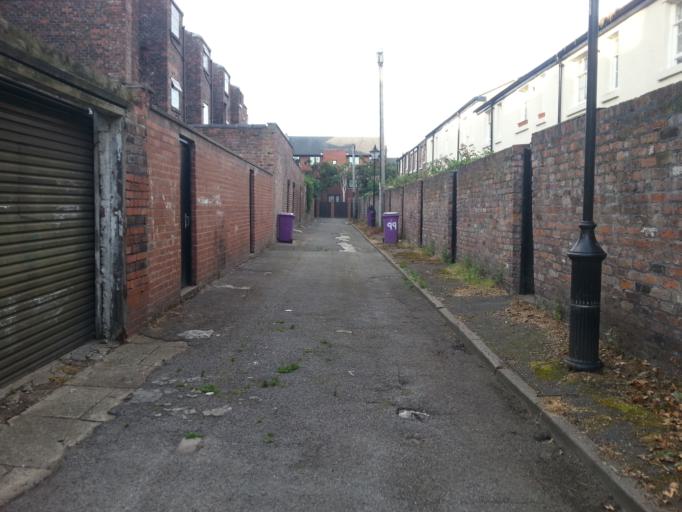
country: GB
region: England
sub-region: Liverpool
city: Liverpool
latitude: 53.3969
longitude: -2.9675
